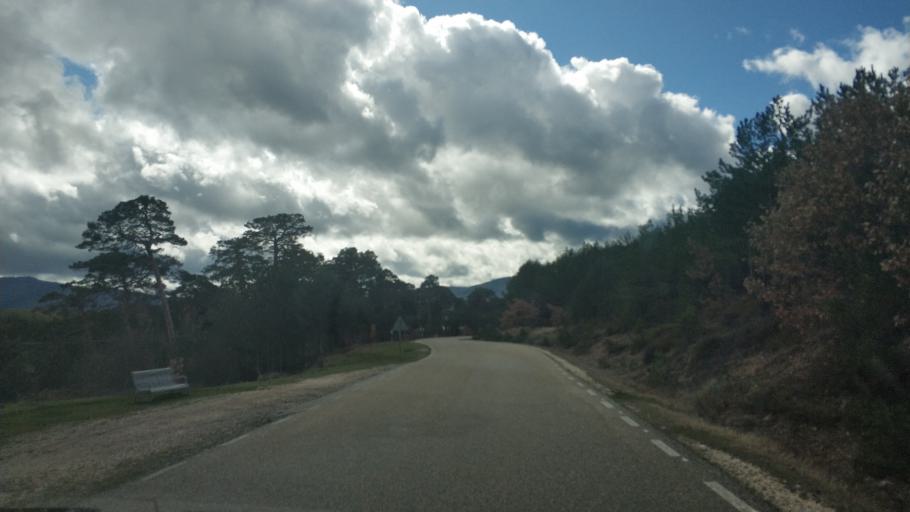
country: ES
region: Castille and Leon
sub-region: Provincia de Burgos
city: Quintanar de la Sierra
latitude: 41.9913
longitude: -3.0263
